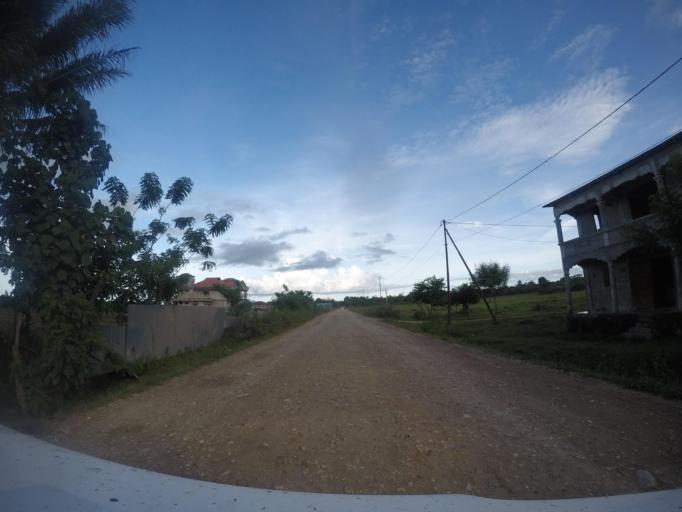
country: TL
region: Lautem
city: Lospalos
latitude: -8.5095
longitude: 126.9986
